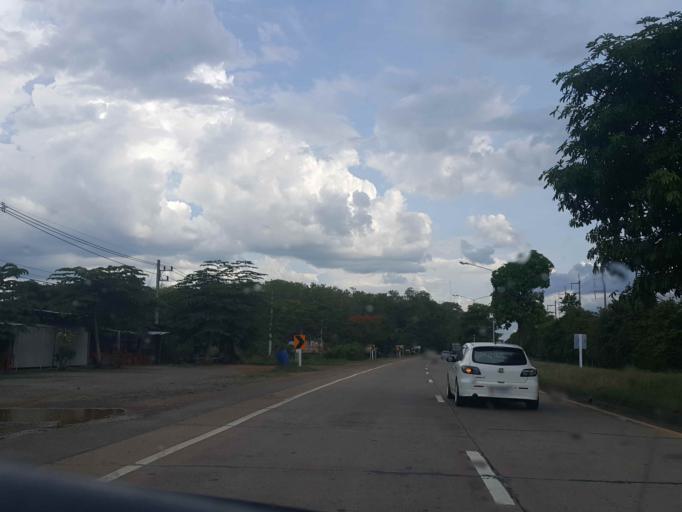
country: TH
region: Phrae
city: Den Chai
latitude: 17.9901
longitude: 100.0972
